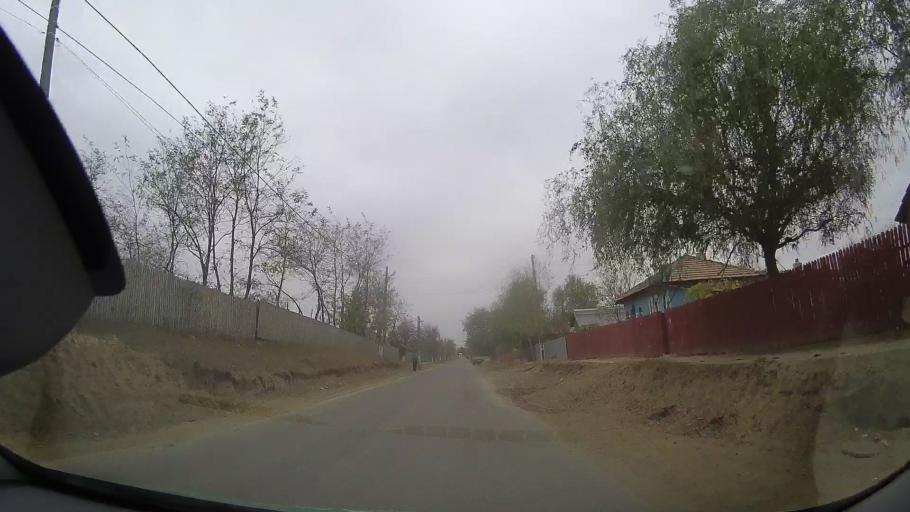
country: RO
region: Buzau
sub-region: Comuna Luciu
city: Luciu
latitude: 44.9684
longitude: 27.0913
